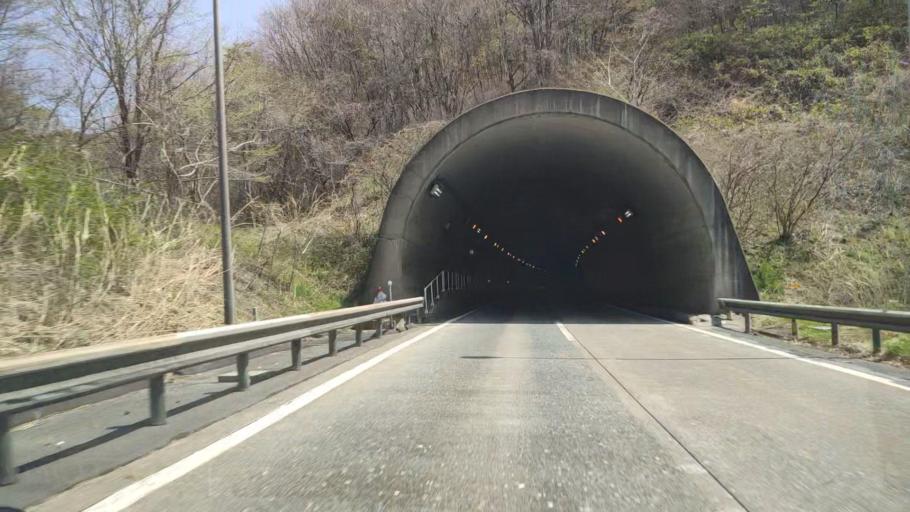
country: JP
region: Iwate
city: Ichinohe
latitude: 40.2300
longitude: 141.3740
